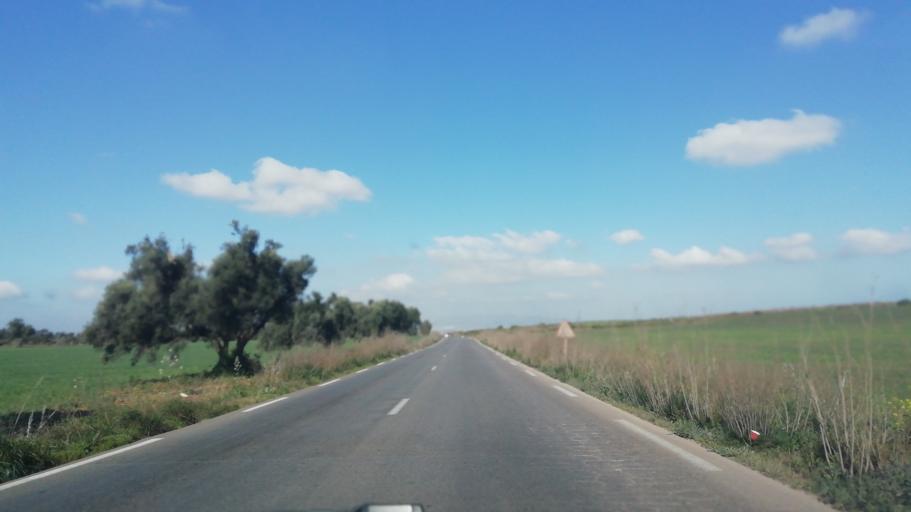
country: DZ
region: Oran
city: Ain el Bya
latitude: 35.7178
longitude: -0.2357
